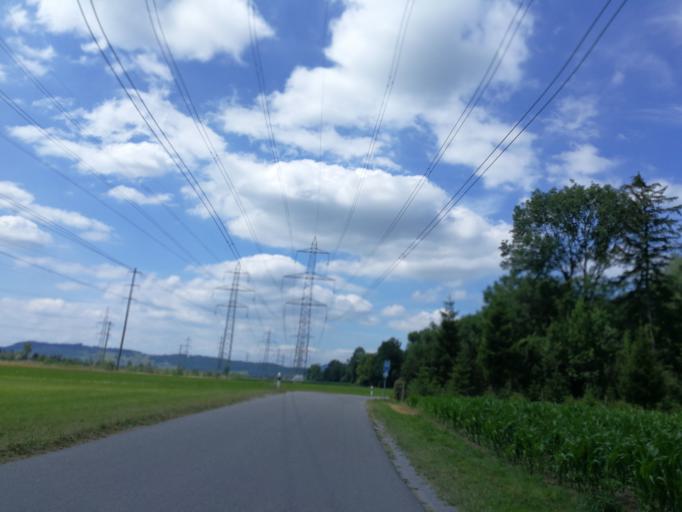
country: CH
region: Saint Gallen
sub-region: Wahlkreis See-Gaster
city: Benken
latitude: 47.1748
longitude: 9.0068
